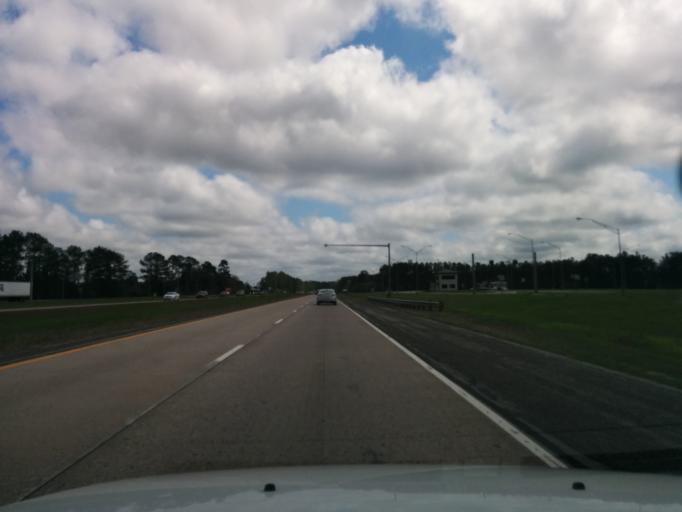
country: US
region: Georgia
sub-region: Chatham County
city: Bloomingdale
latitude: 32.1693
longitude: -81.4448
